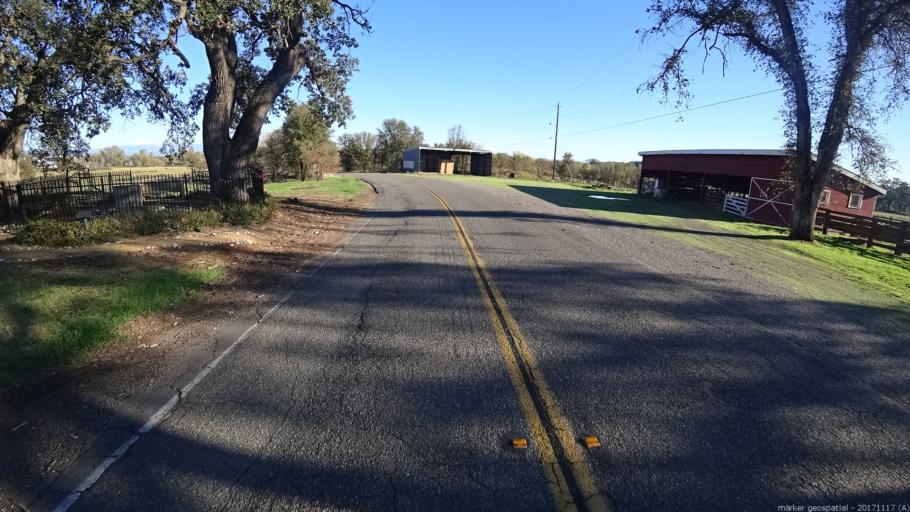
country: US
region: California
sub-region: Shasta County
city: Cottonwood
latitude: 40.3923
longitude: -122.2129
